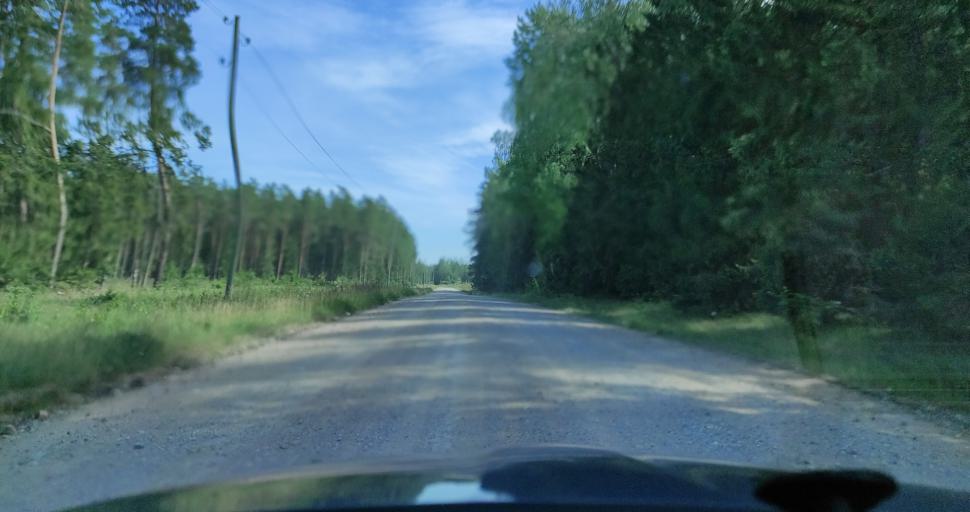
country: LV
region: Durbe
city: Liegi
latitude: 56.7626
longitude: 21.3188
